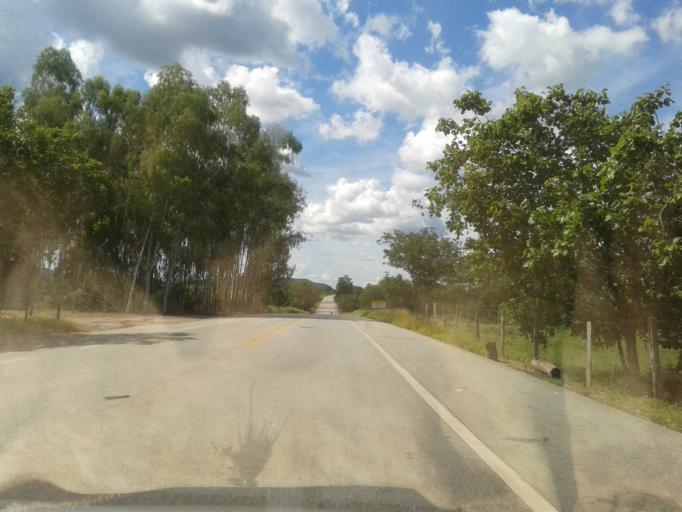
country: BR
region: Goias
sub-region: Itapuranga
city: Itapuranga
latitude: -15.5735
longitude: -50.2756
